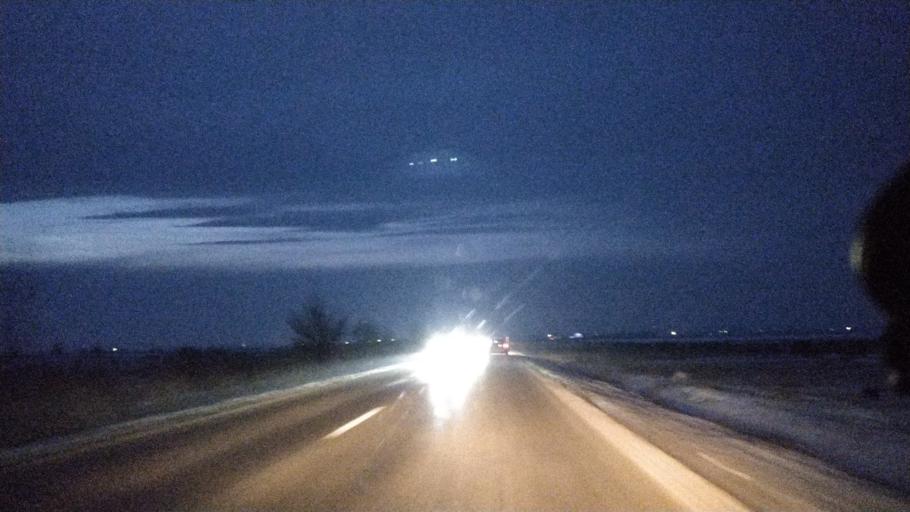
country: RO
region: Vrancea
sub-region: Comuna Milcovul
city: Milcovul
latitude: 45.6721
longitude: 27.2579
